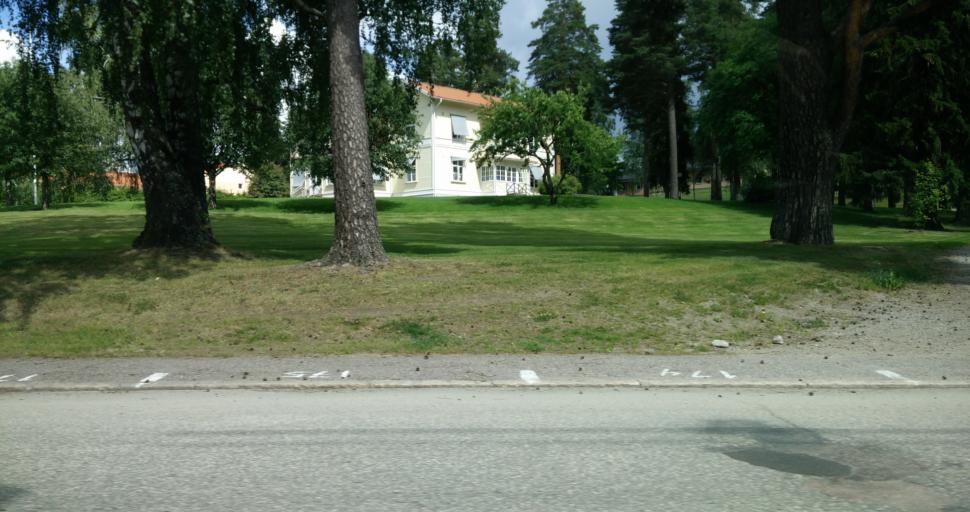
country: SE
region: Vaermland
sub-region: Hagfors Kommun
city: Hagfors
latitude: 60.0290
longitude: 13.6974
